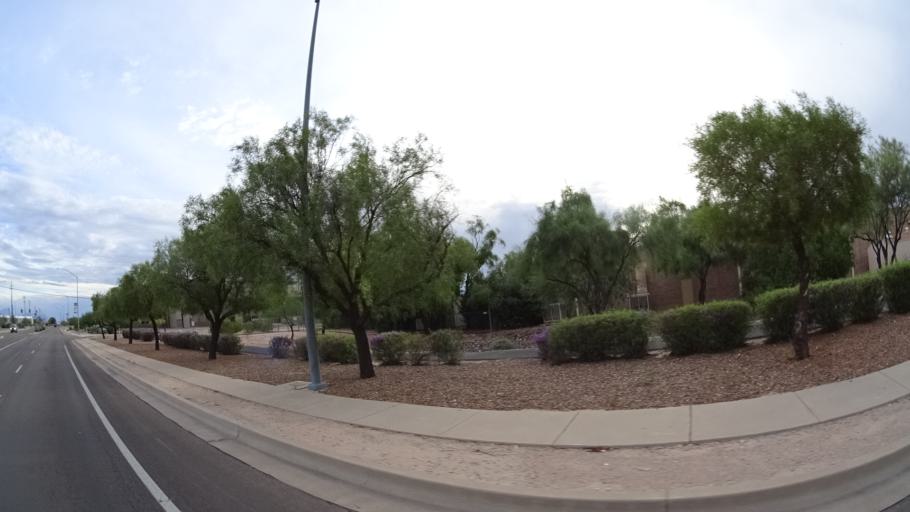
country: US
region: Arizona
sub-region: Pima County
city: South Tucson
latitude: 32.1403
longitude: -110.9349
